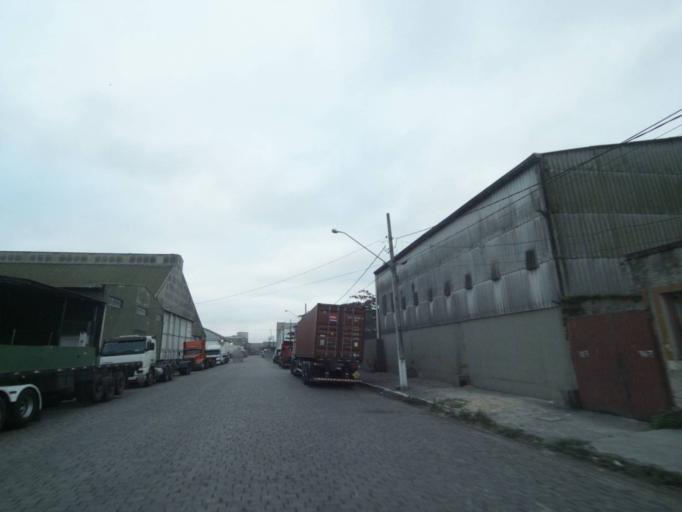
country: BR
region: Parana
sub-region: Paranagua
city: Paranagua
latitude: -25.5113
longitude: -48.5177
